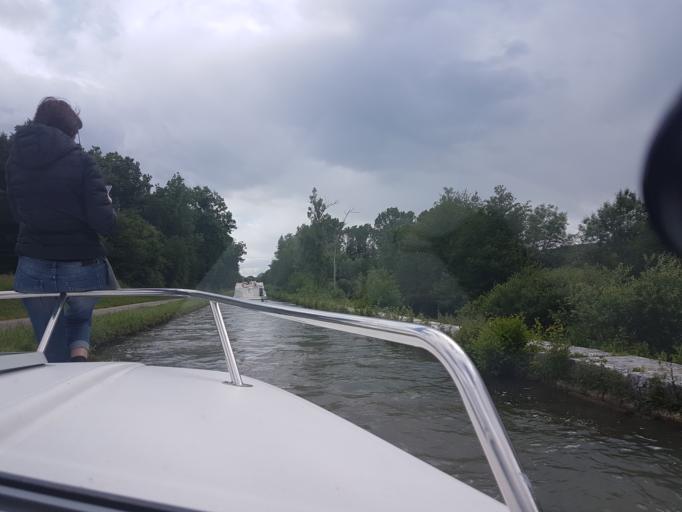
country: FR
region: Bourgogne
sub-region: Departement de l'Yonne
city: Vermenton
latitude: 47.5560
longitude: 3.6338
